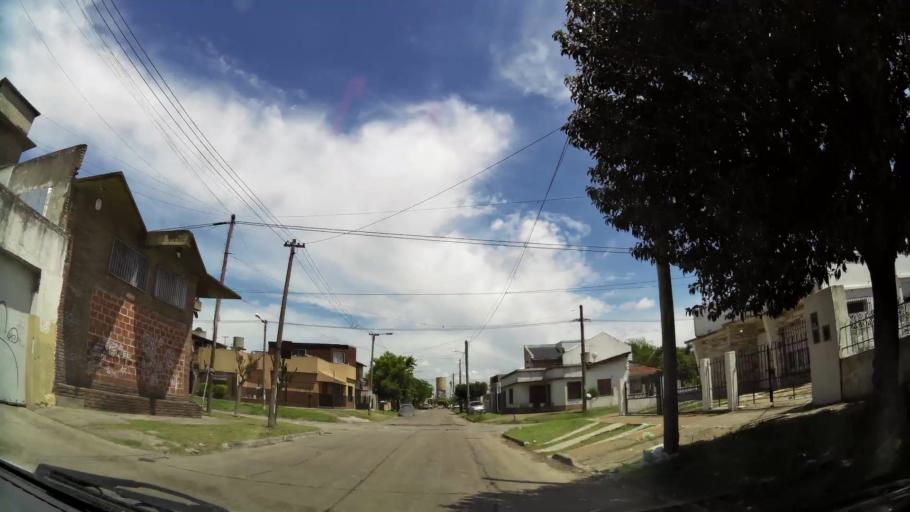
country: AR
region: Buenos Aires
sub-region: Partido de Quilmes
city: Quilmes
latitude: -34.7797
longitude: -58.2695
